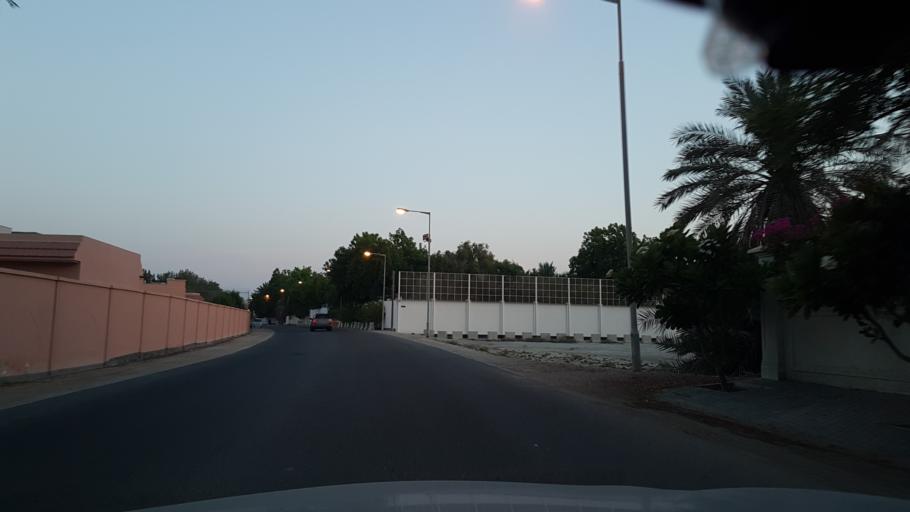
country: BH
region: Manama
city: Jidd Hafs
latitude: 26.2282
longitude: 50.4888
